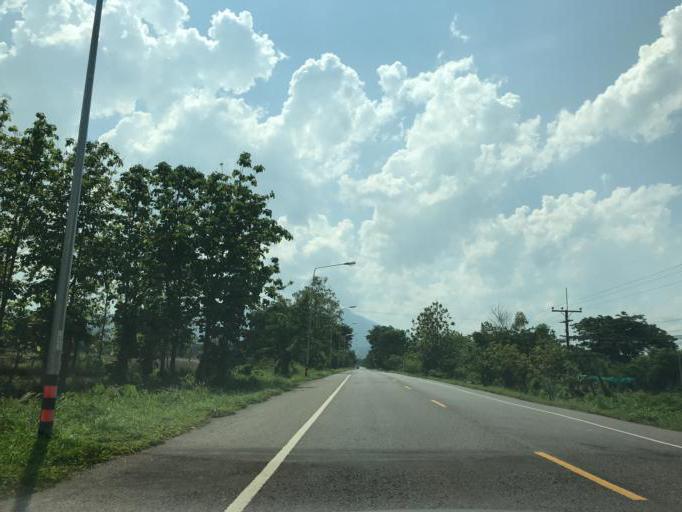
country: TH
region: Phayao
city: Phayao
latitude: 19.0814
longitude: 99.8621
